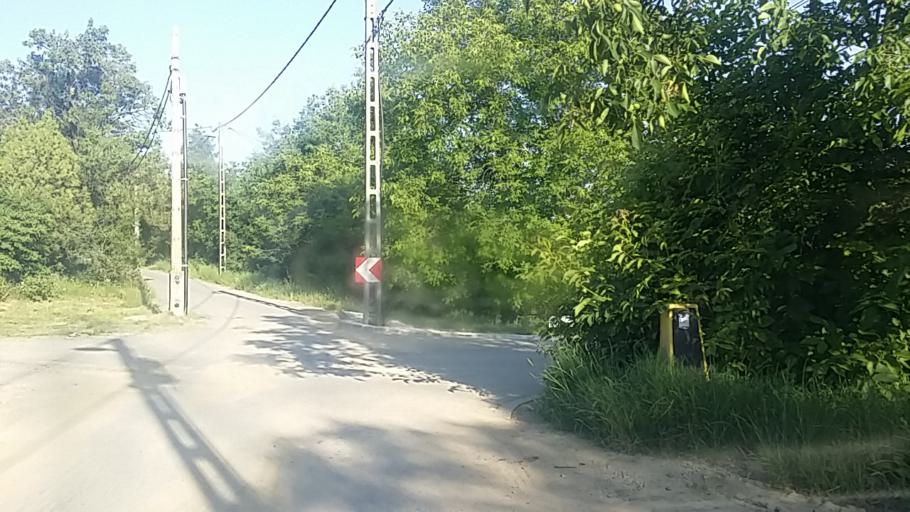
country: HU
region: Pest
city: Urom
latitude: 47.5786
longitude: 19.0167
